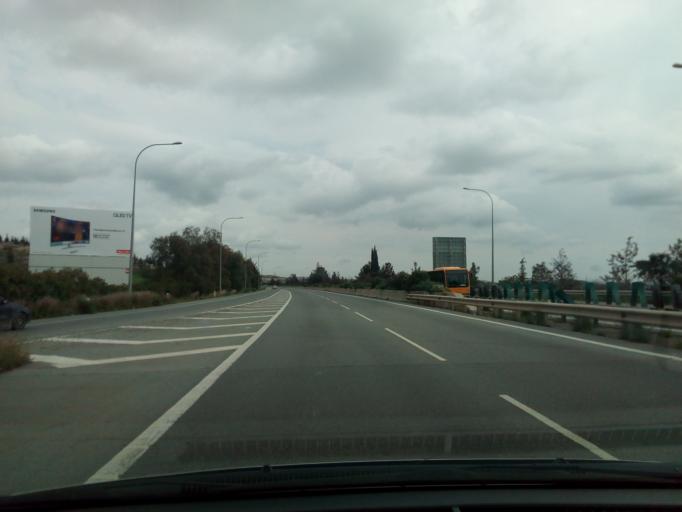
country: CY
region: Lefkosia
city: Alampra
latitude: 35.0013
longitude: 33.3992
